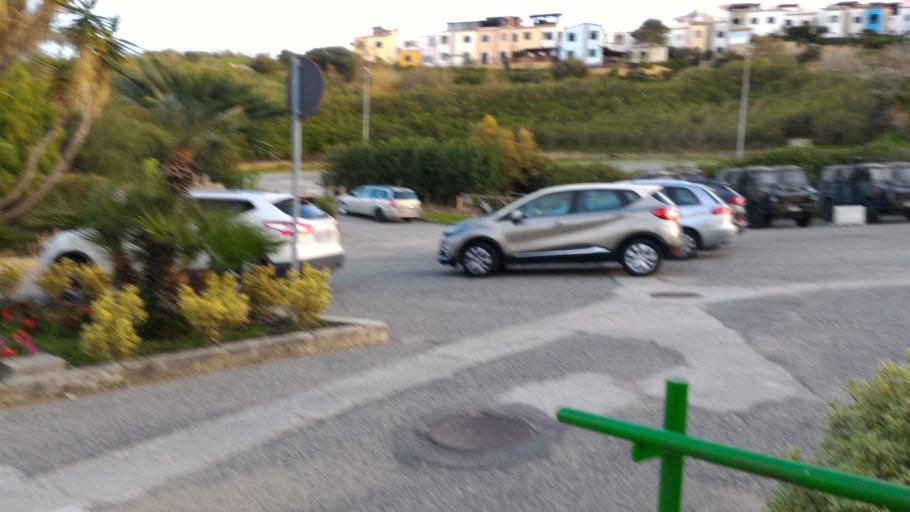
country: IT
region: Calabria
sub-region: Provincia di Crotone
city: Crotone
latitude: 39.0417
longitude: 17.1525
